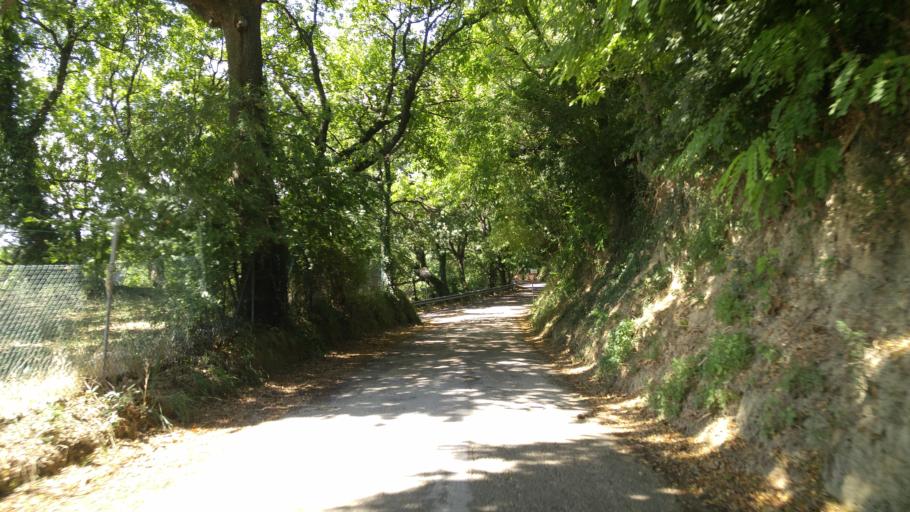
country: IT
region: The Marches
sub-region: Provincia di Pesaro e Urbino
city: Cuccurano
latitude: 43.8158
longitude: 12.9698
